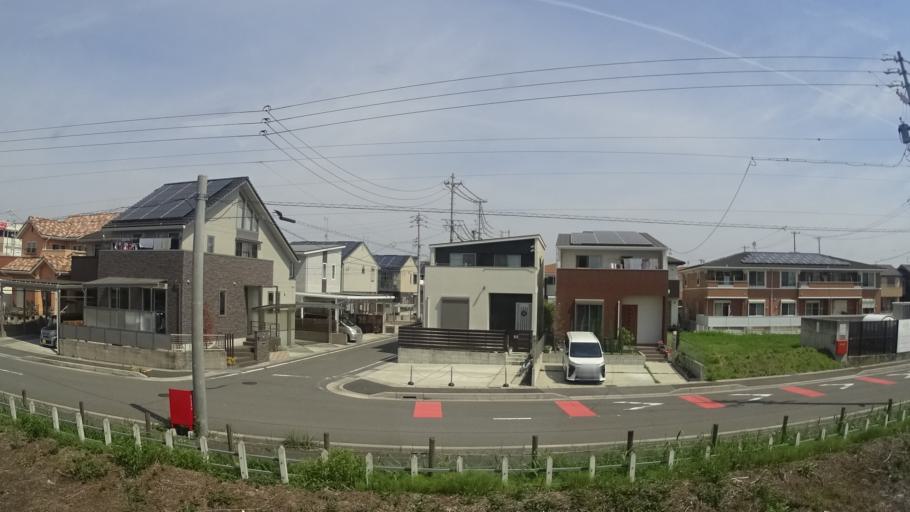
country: JP
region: Aichi
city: Kanie
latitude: 35.1427
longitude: 136.7985
